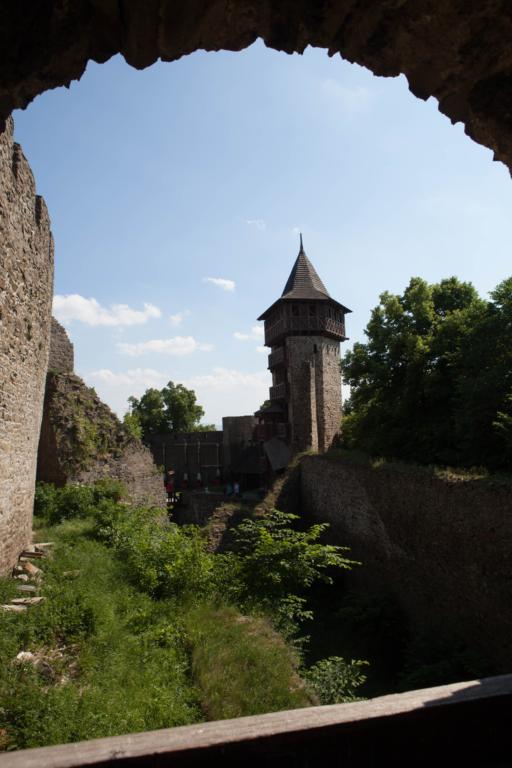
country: CZ
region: Olomoucky
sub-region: Okres Prerov
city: Lipnik nad Becvou
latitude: 49.5174
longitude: 17.6301
